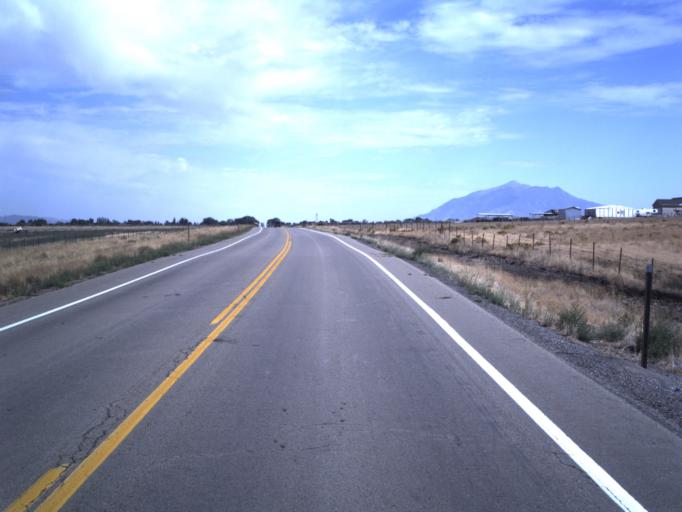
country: US
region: Utah
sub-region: Juab County
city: Nephi
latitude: 39.5335
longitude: -111.8637
